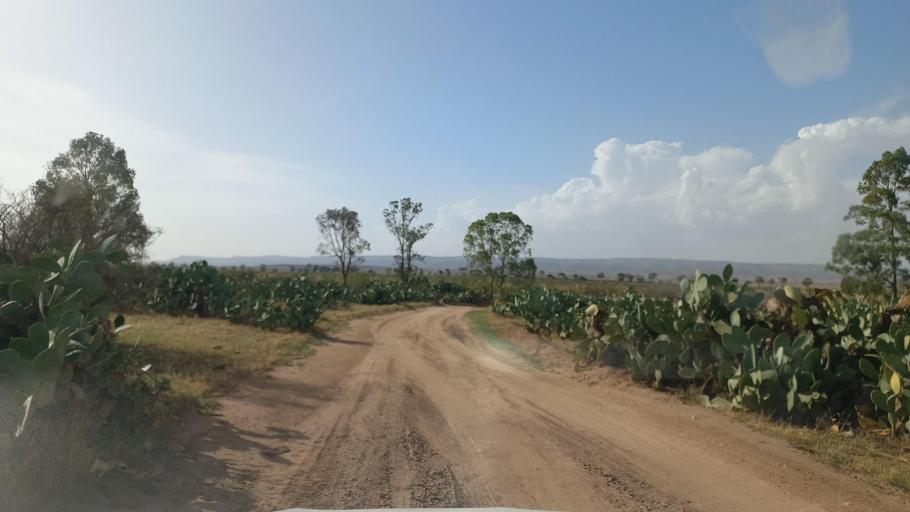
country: TN
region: Al Qasrayn
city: Kasserine
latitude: 35.2263
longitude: 8.9685
